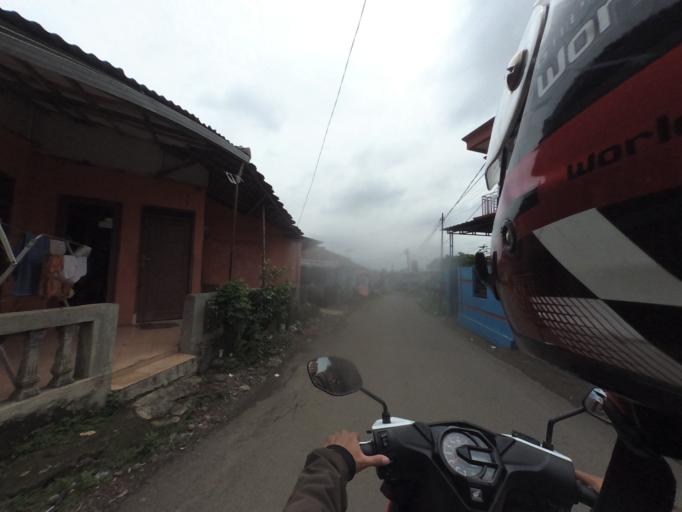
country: ID
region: West Java
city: Bogor
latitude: -6.6085
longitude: 106.7570
